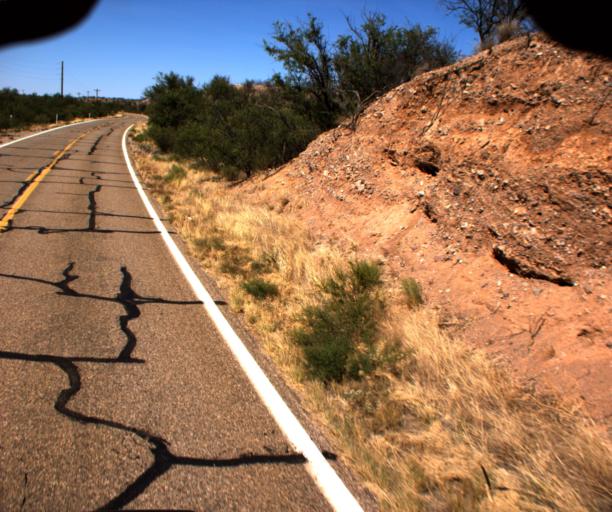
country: US
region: Arizona
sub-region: Pima County
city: Three Points
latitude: 31.8664
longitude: -111.3969
